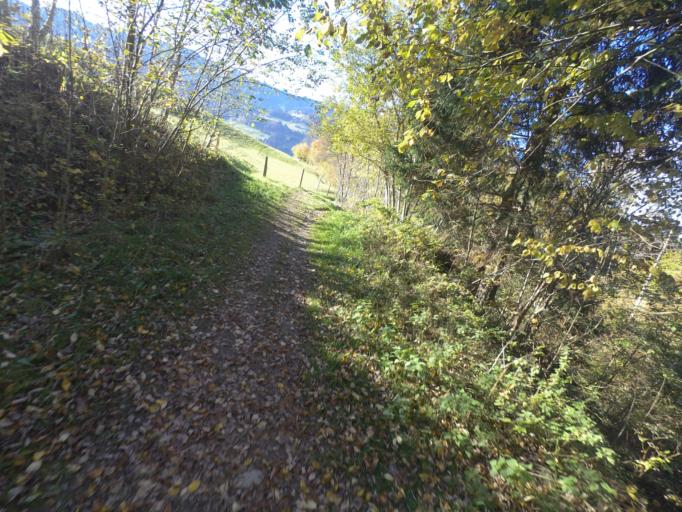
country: AT
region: Salzburg
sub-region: Politischer Bezirk Sankt Johann im Pongau
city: Sankt Johann im Pongau
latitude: 47.3472
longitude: 13.2161
